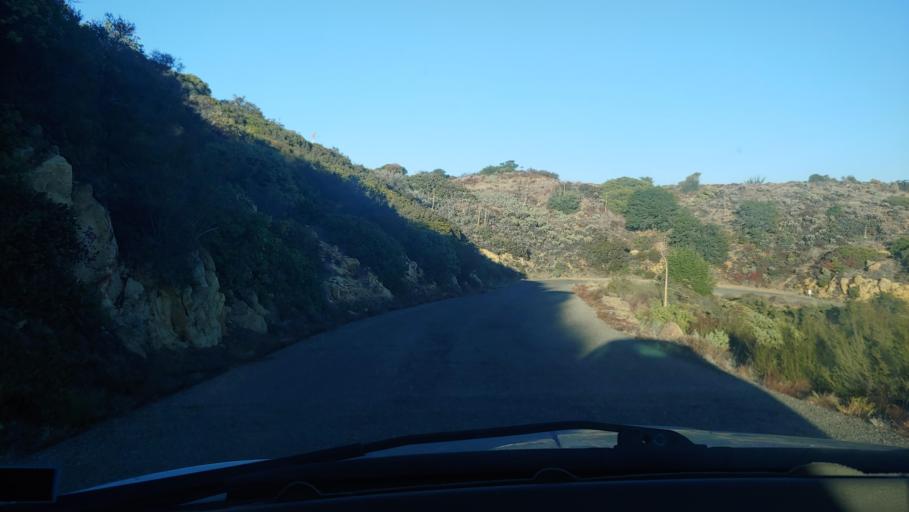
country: US
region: California
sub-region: Santa Barbara County
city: Mission Canyon
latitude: 34.5084
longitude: -119.7701
